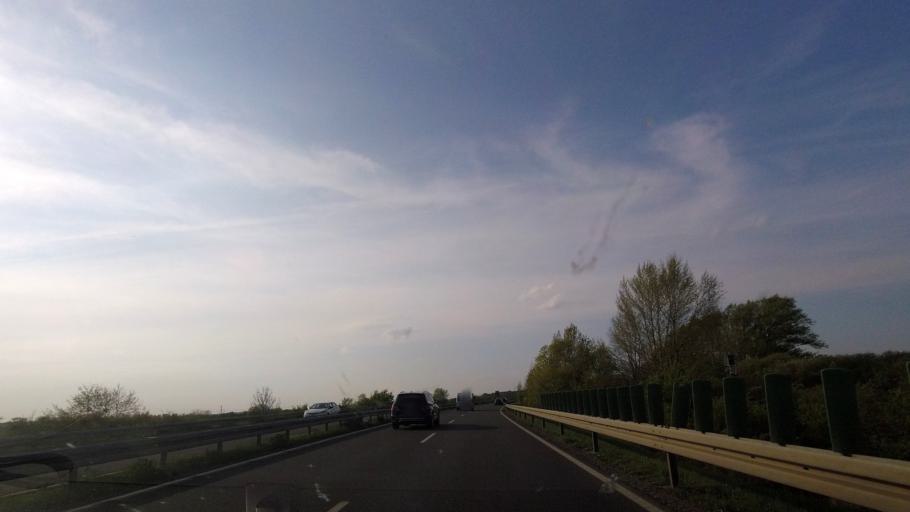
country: DE
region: Saxony-Anhalt
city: Wittenburg
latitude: 51.8330
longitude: 12.6300
